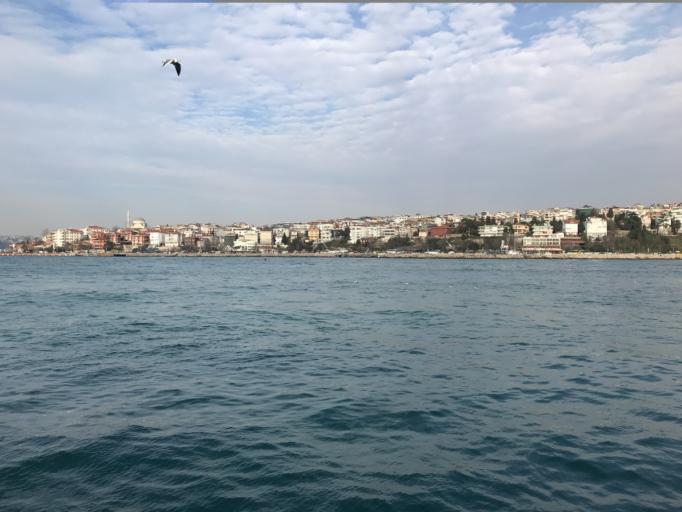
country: TR
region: Istanbul
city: UEskuedar
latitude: 41.0165
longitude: 29.0038
